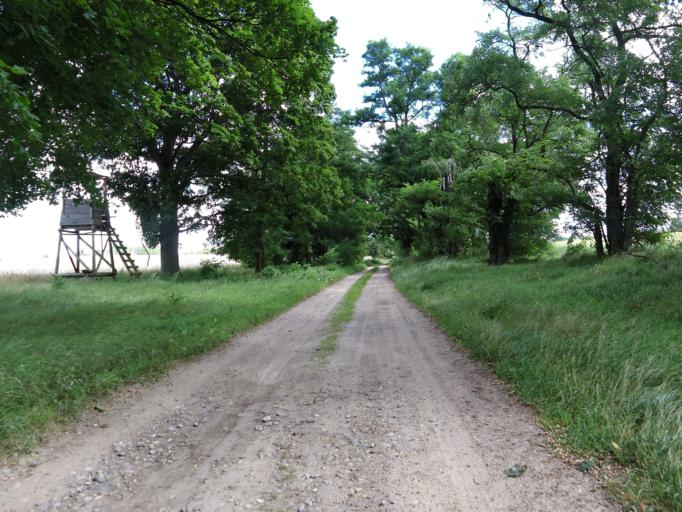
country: DE
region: Brandenburg
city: Lychen
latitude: 53.2283
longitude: 13.3363
